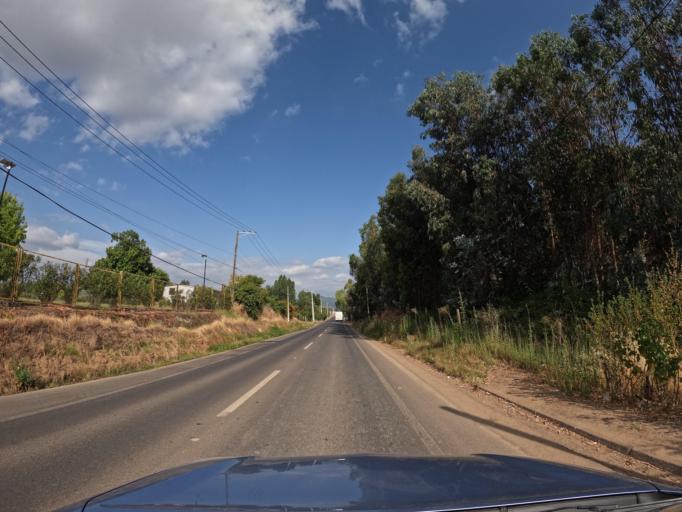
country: CL
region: Maule
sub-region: Provincia de Curico
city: Molina
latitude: -35.2748
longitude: -71.2940
